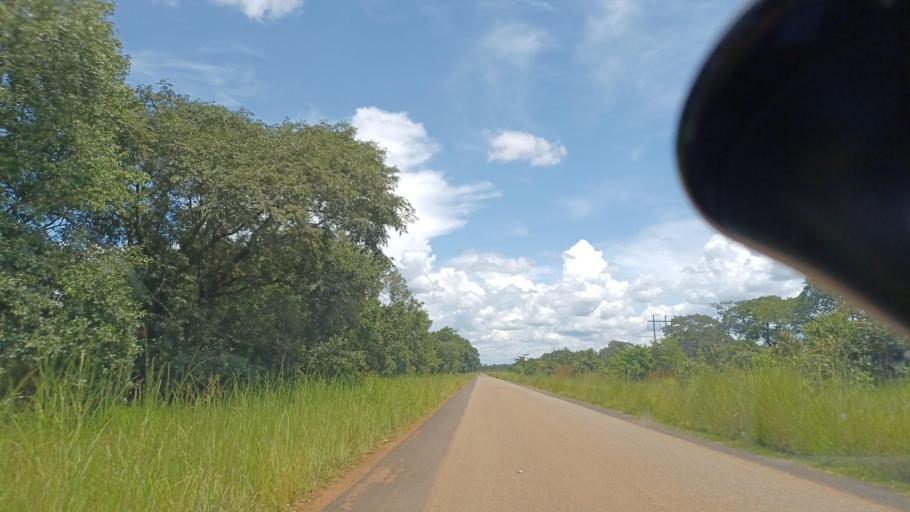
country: ZM
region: North-Western
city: Solwezi
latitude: -12.5707
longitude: 26.1358
